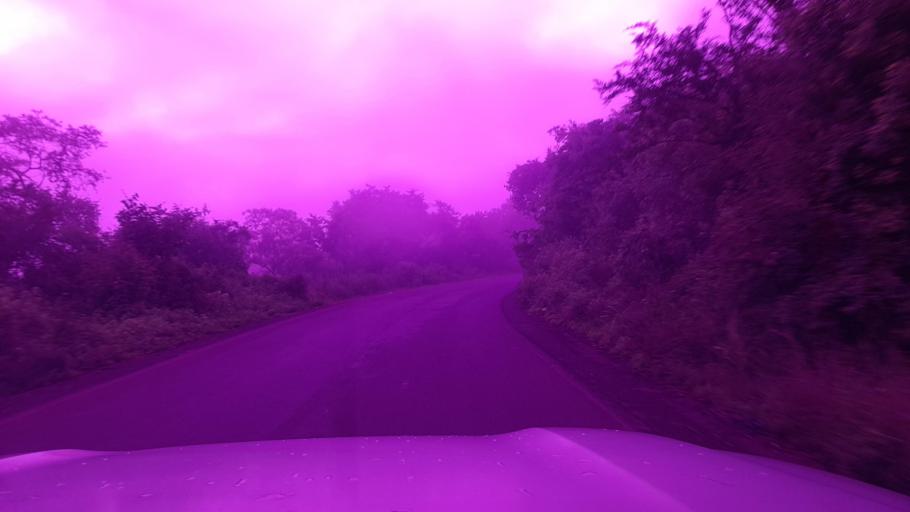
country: ET
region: Oromiya
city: Waliso
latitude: 8.1761
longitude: 37.5580
